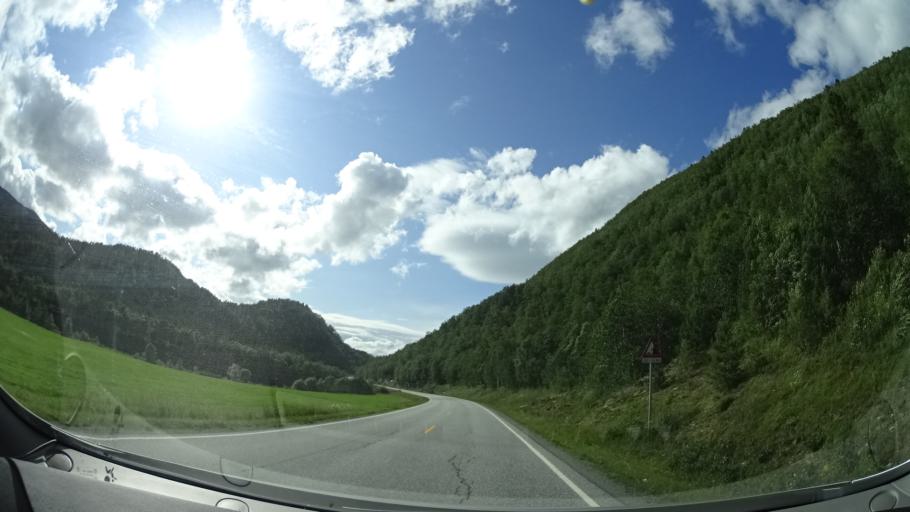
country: NO
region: Sor-Trondelag
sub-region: Hemne
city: Kyrksaeterora
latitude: 63.2105
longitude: 9.1579
